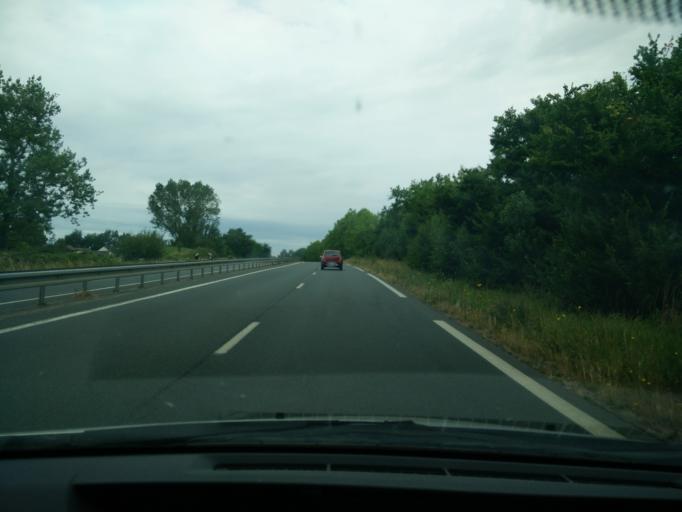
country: FR
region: Pays de la Loire
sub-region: Departement de Maine-et-Loire
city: Brissac-Quince
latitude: 47.3500
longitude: -0.4375
